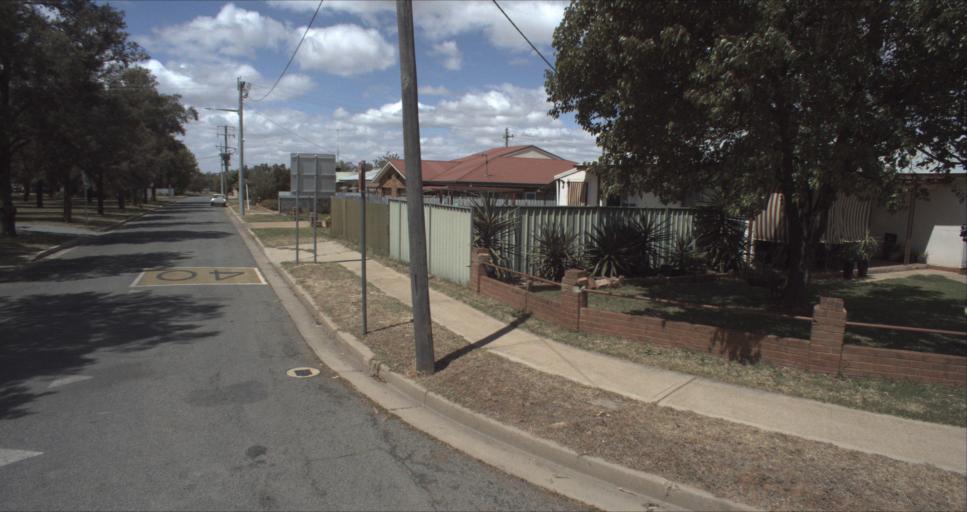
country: AU
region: New South Wales
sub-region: Leeton
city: Leeton
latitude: -34.5620
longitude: 146.3974
